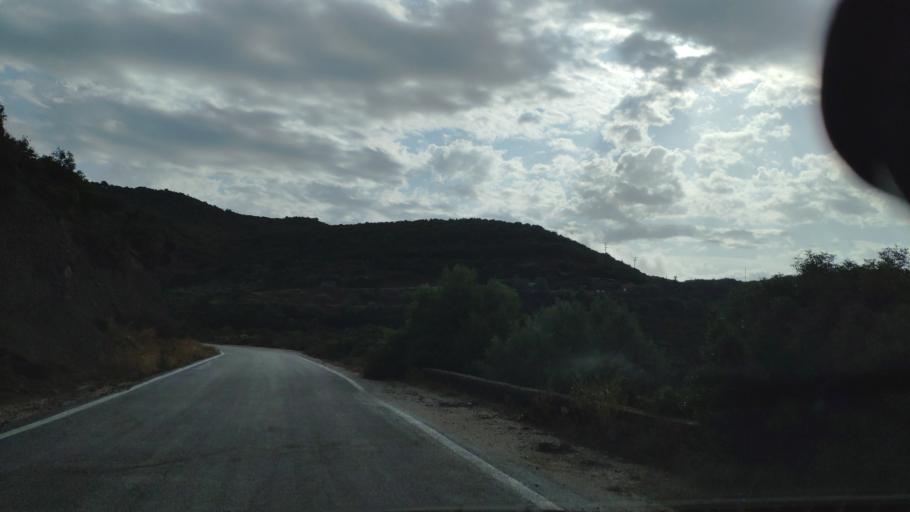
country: GR
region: West Greece
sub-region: Nomos Aitolias kai Akarnanias
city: Sardinia
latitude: 38.8895
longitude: 21.2296
